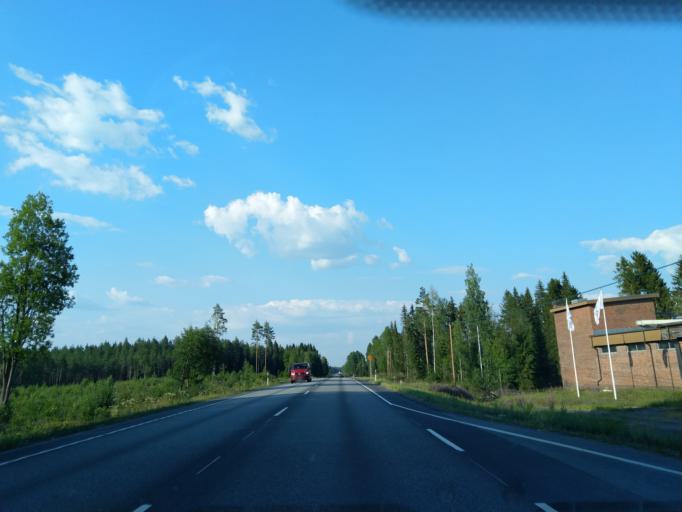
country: FI
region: Satakunta
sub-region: Pori
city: Pomarkku
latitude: 61.7282
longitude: 22.0672
